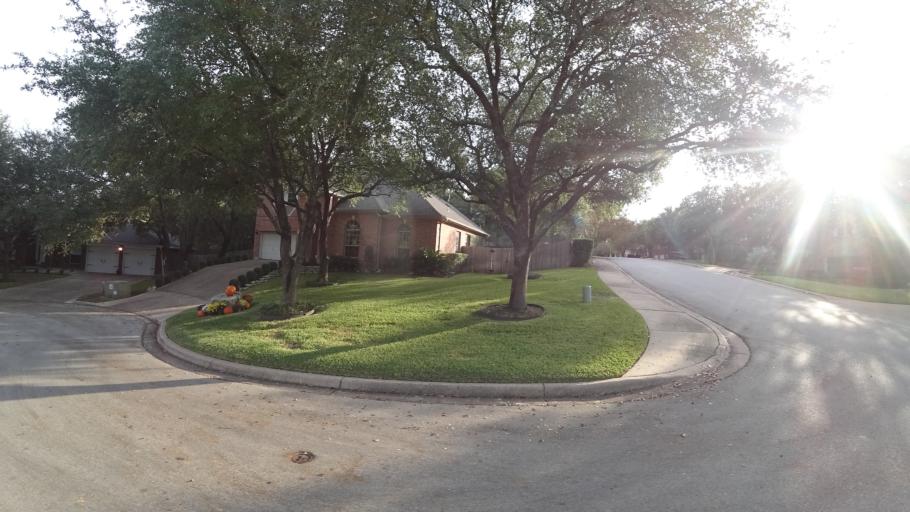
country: US
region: Texas
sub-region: Travis County
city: Hudson Bend
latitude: 30.3789
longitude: -97.8879
